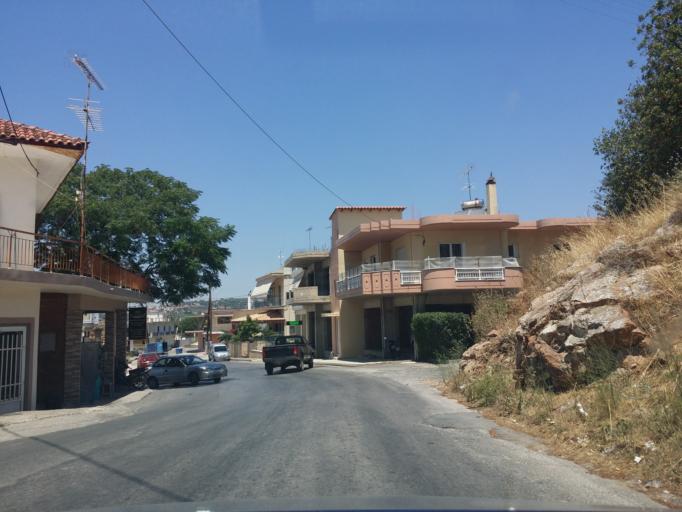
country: GR
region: Peloponnese
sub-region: Nomos Lakonias
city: Vlakhiotis
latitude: 36.8621
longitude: 22.7125
